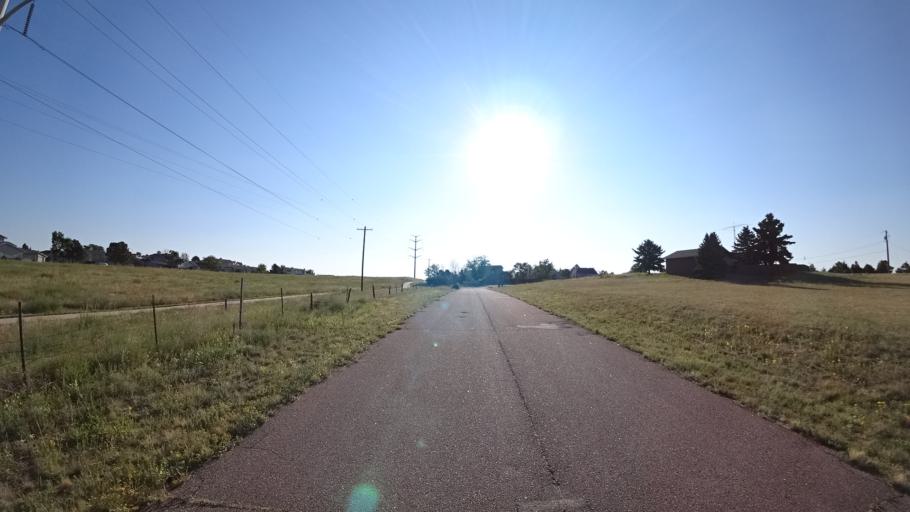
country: US
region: Colorado
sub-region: El Paso County
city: Black Forest
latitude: 38.9403
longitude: -104.7672
